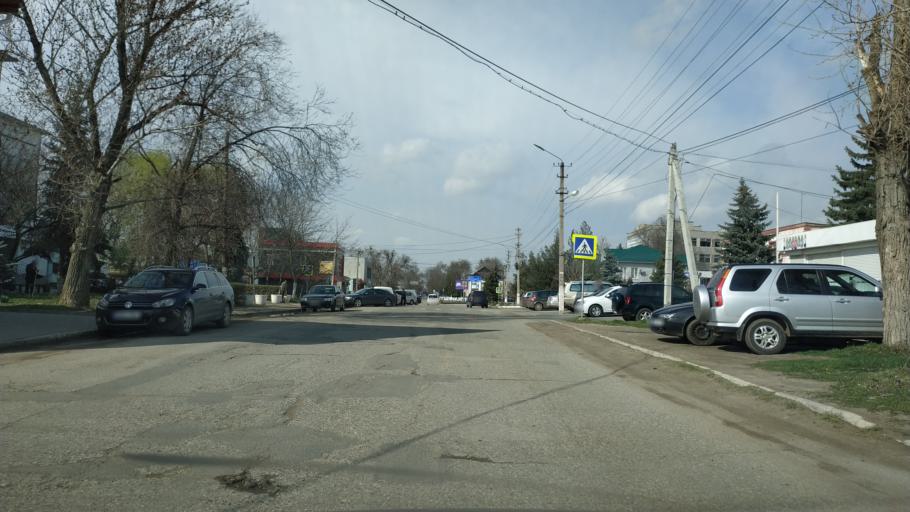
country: MD
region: Gagauzia
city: Vulcanesti
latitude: 45.6821
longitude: 28.4076
